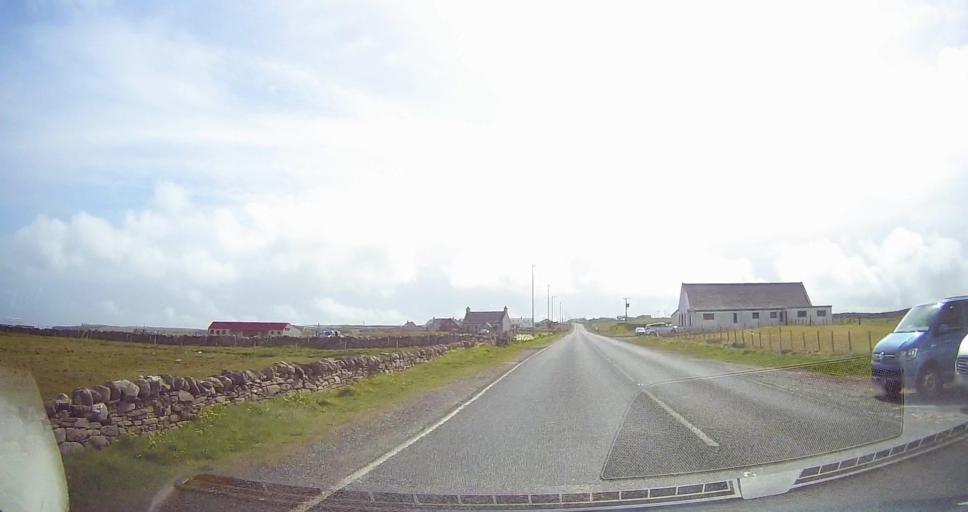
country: GB
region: Scotland
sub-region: Shetland Islands
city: Sandwick
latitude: 59.9258
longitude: -1.2974
